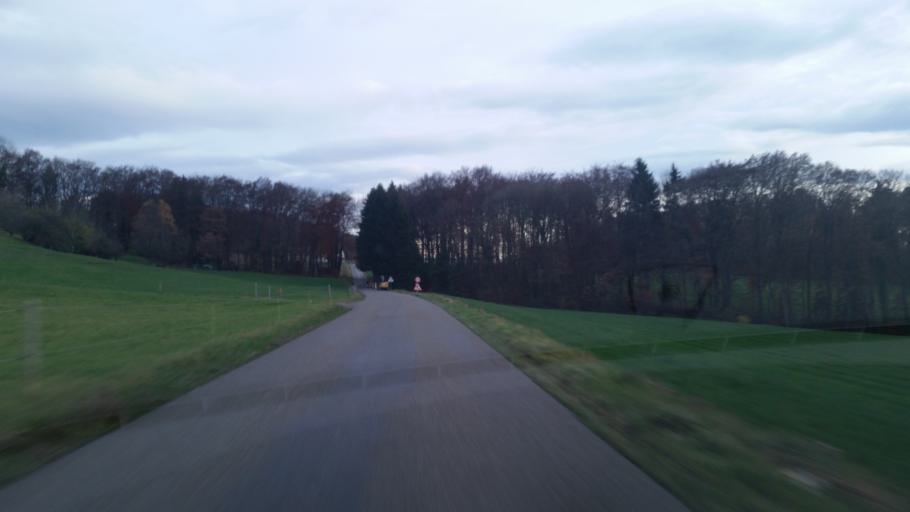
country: CH
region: Aargau
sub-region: Bezirk Baden
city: Kunten
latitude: 47.3857
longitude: 8.3380
